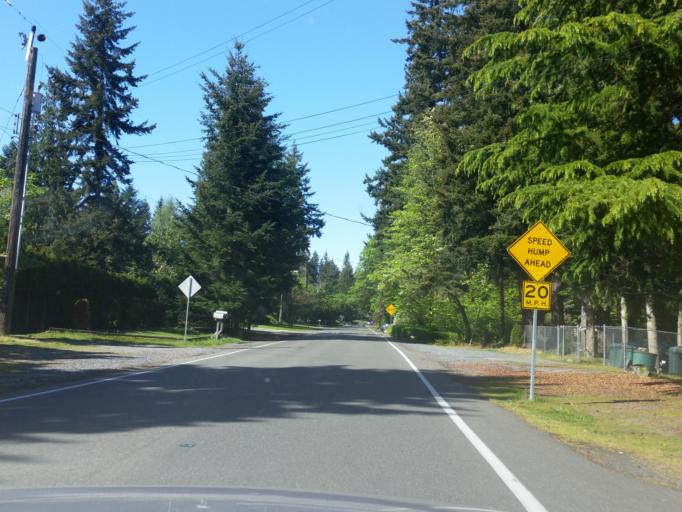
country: US
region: Washington
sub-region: King County
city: Shoreline
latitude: 47.7655
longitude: -122.3487
